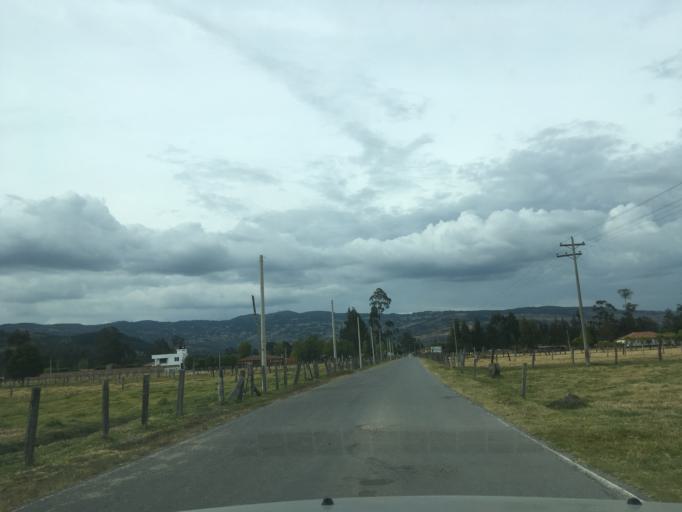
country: CO
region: Boyaca
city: Firavitoba
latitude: 5.6539
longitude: -72.9893
